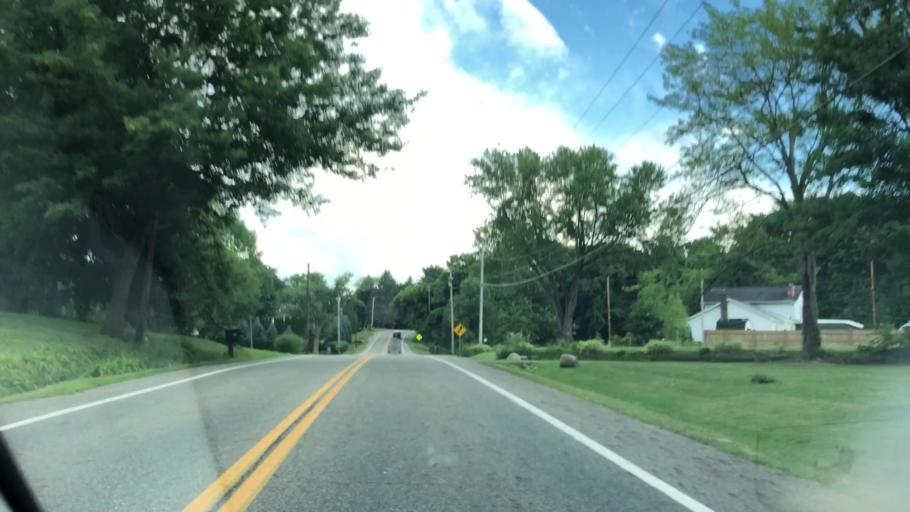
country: US
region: Ohio
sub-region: Summit County
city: Portage Lakes
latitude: 40.9921
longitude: -81.5514
